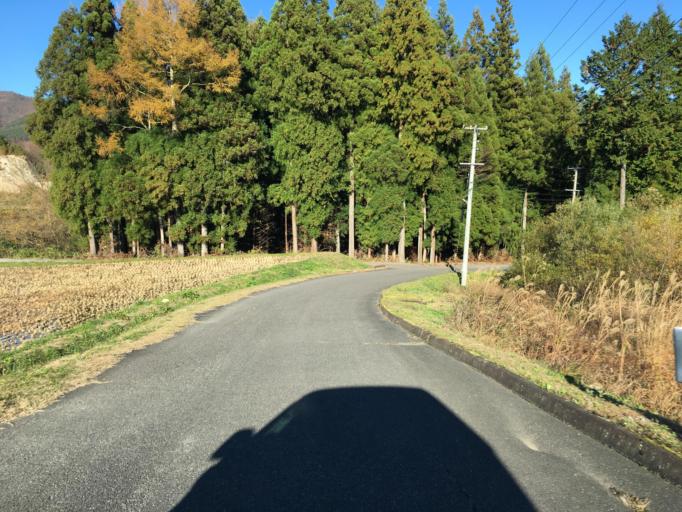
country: JP
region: Fukushima
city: Ishikawa
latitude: 37.2418
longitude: 140.5312
